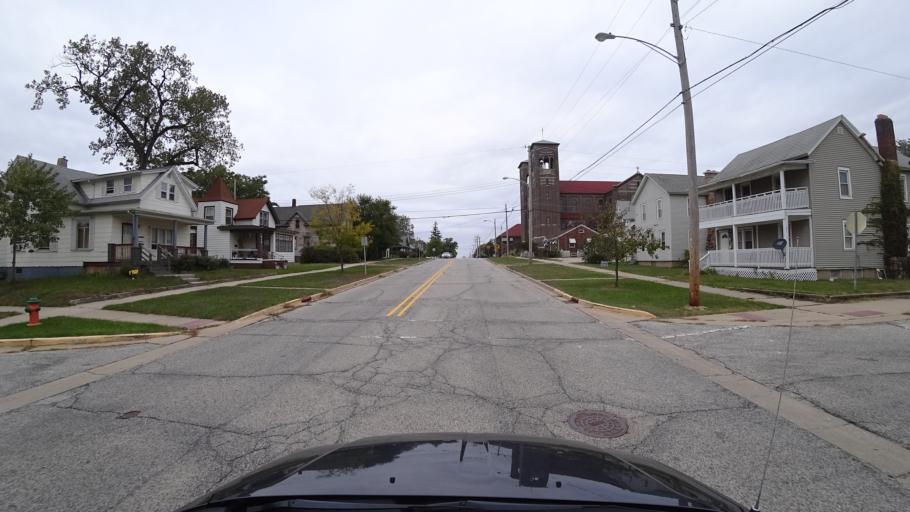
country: US
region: Indiana
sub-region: LaPorte County
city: Michigan City
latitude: 41.7067
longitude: -86.8982
